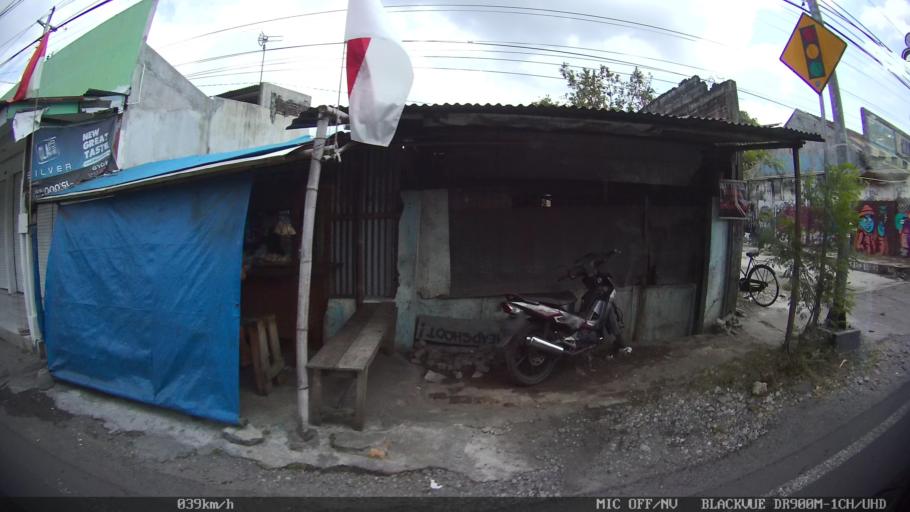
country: ID
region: Daerah Istimewa Yogyakarta
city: Gamping Lor
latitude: -7.8004
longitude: 110.3313
